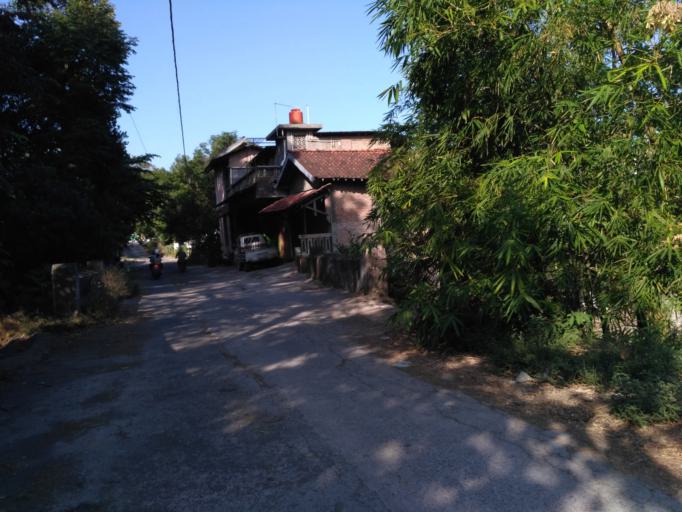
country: ID
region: Daerah Istimewa Yogyakarta
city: Depok
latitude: -7.7729
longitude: 110.4297
